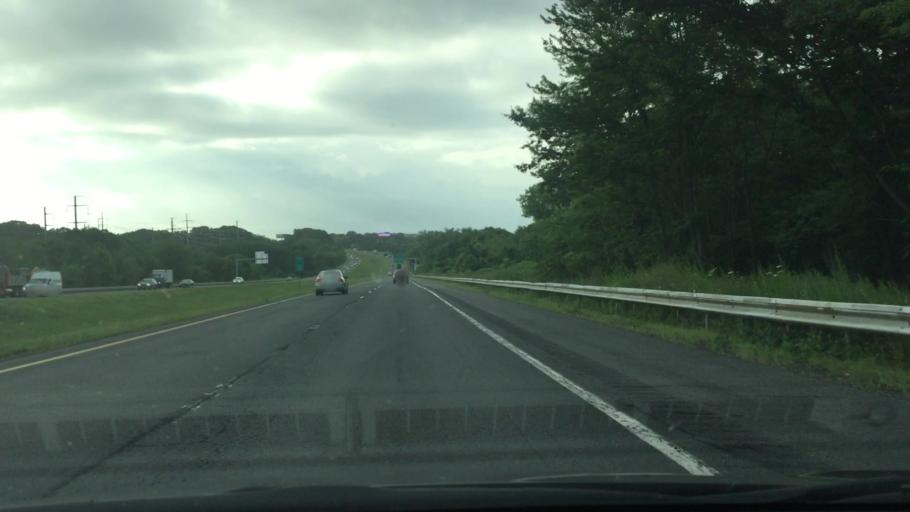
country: US
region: Massachusetts
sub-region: Hampden County
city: North Chicopee
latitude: 42.1668
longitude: -72.5639
